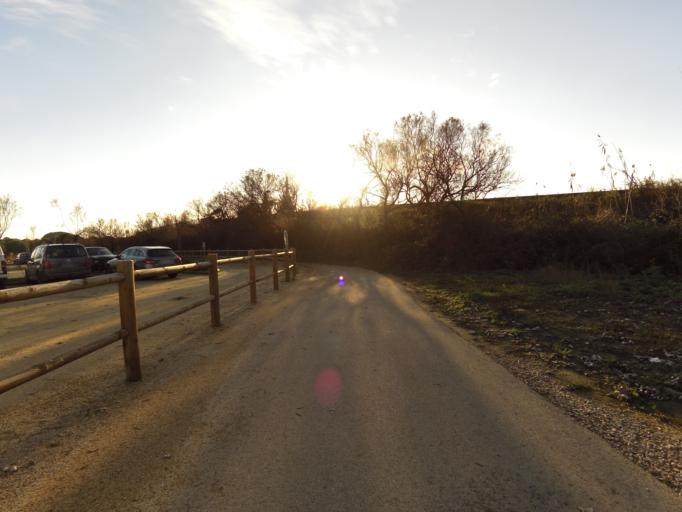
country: FR
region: Languedoc-Roussillon
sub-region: Departement du Gard
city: Aigues-Mortes
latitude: 43.5888
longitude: 4.2106
